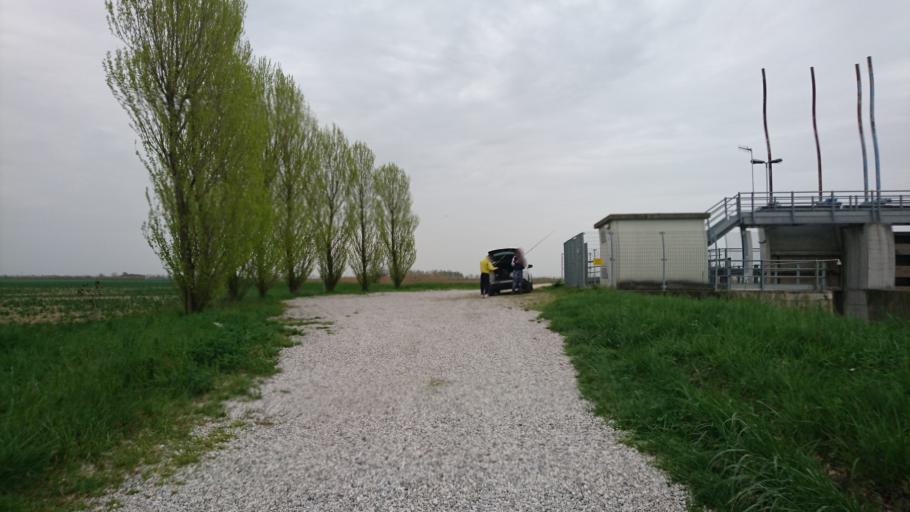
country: IT
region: Veneto
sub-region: Provincia di Venezia
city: Lugugnana
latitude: 45.6840
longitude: 12.9527
